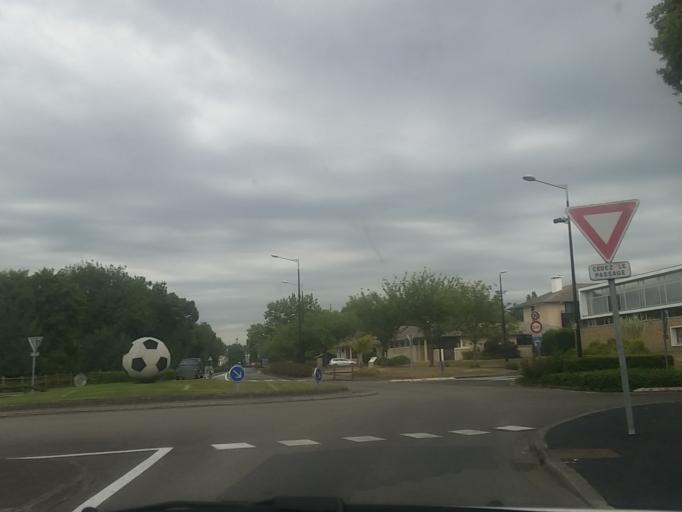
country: FR
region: Pays de la Loire
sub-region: Departement de la Loire-Atlantique
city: Saint-Sebastien-sur-Loire
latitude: 47.2111
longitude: -1.4961
